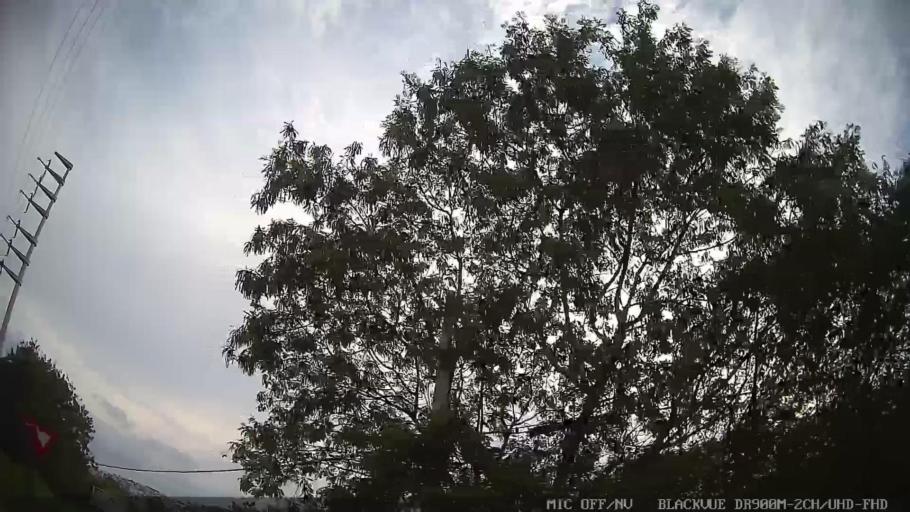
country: BR
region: Sao Paulo
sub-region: Braganca Paulista
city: Braganca Paulista
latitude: -22.9347
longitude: -46.5569
